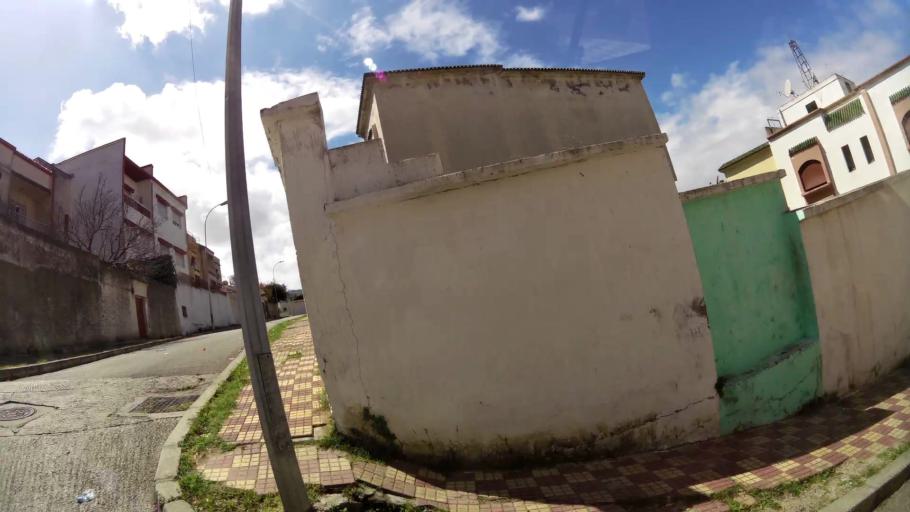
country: MA
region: Tanger-Tetouan
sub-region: Tanger-Assilah
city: Tangier
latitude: 35.7683
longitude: -5.8302
